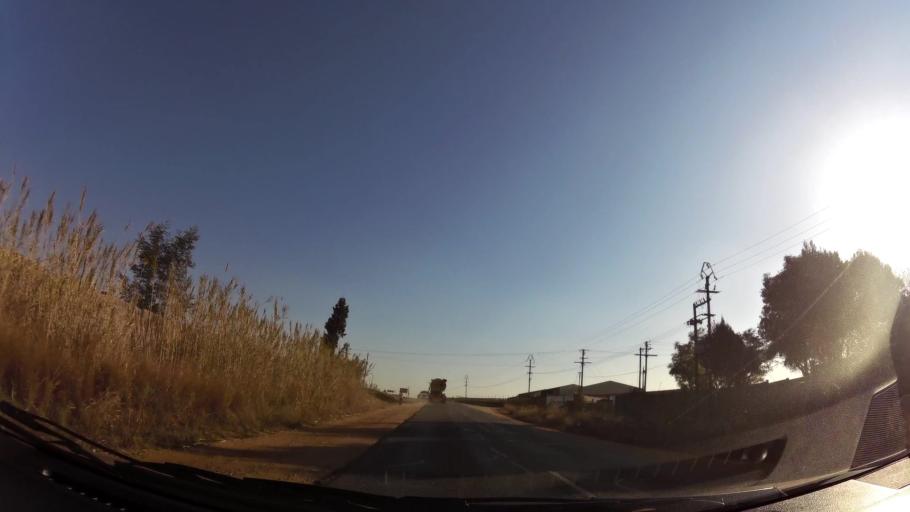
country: ZA
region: Gauteng
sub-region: West Rand District Municipality
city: Muldersdriseloop
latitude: -26.0244
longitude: 27.8715
